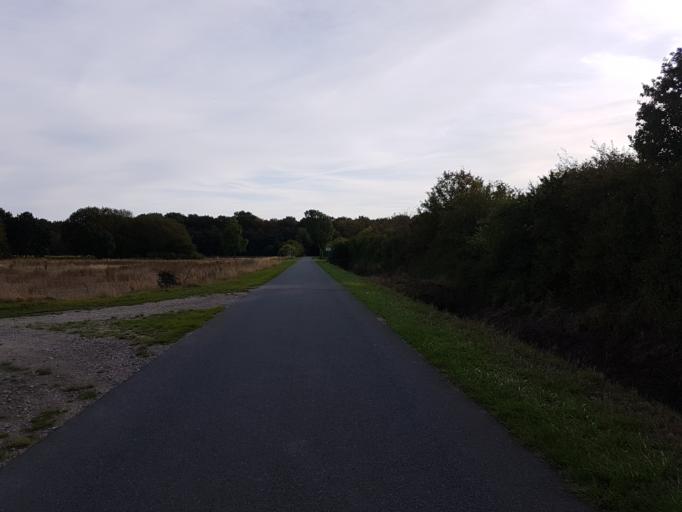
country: DE
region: Lower Saxony
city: Laatzen
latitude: 52.3494
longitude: 9.8687
